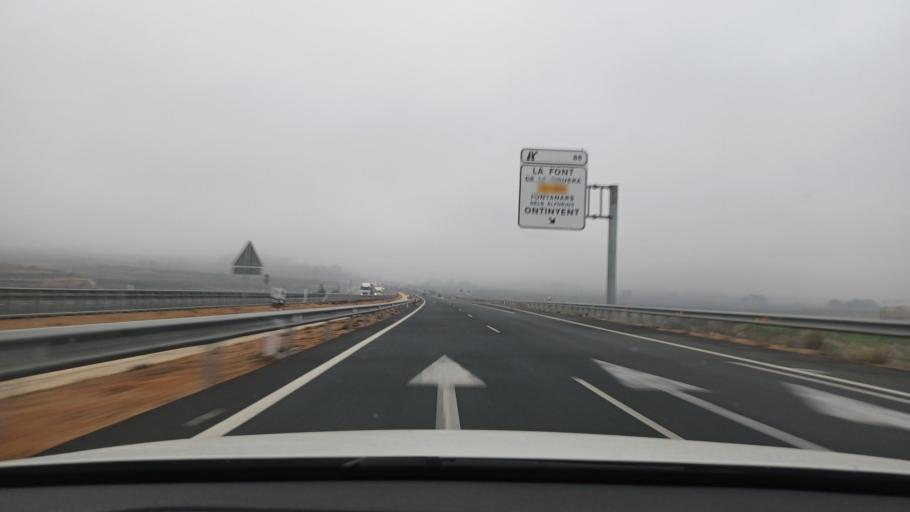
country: ES
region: Valencia
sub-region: Provincia de Valencia
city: La Font de la Figuera
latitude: 38.7889
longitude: -0.8925
